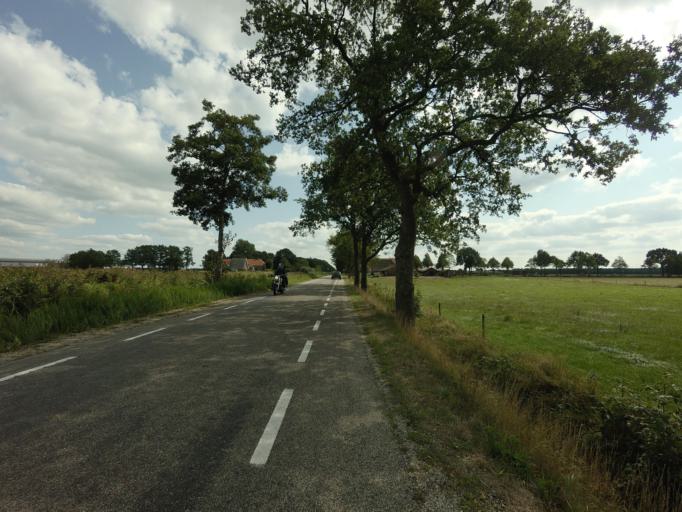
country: NL
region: Drenthe
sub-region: Gemeente Westerveld
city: Dwingeloo
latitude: 52.8724
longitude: 6.4401
